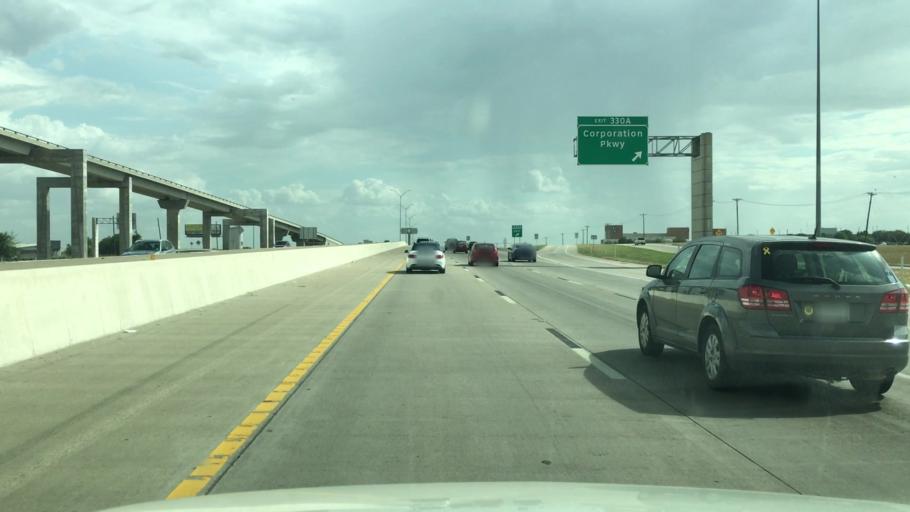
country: US
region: Texas
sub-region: McLennan County
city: Beverly Hills
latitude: 31.4915
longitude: -97.1521
